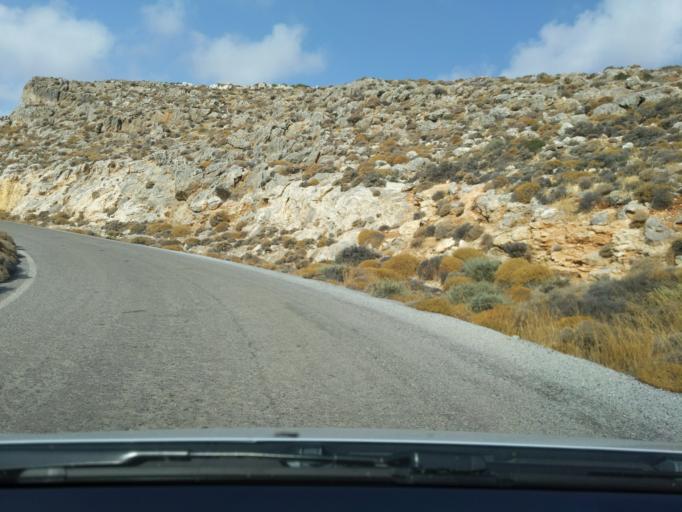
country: GR
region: Crete
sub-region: Nomos Lasithiou
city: Palekastro
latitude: 35.0849
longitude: 26.2612
